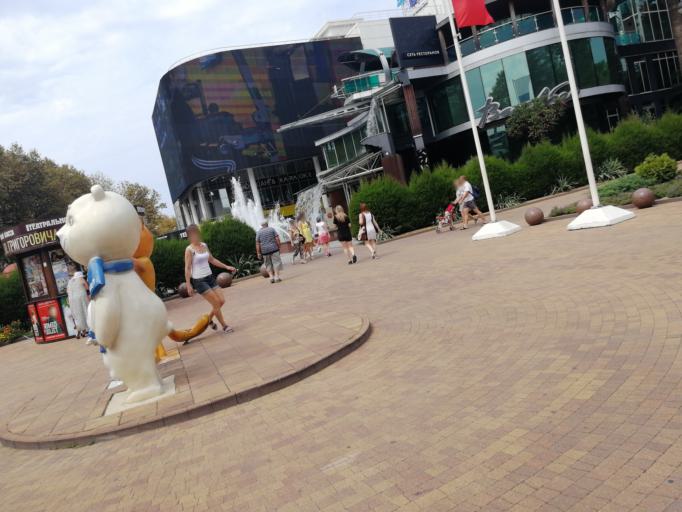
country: RU
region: Krasnodarskiy
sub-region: Sochi City
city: Sochi
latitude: 43.5838
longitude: 39.7208
